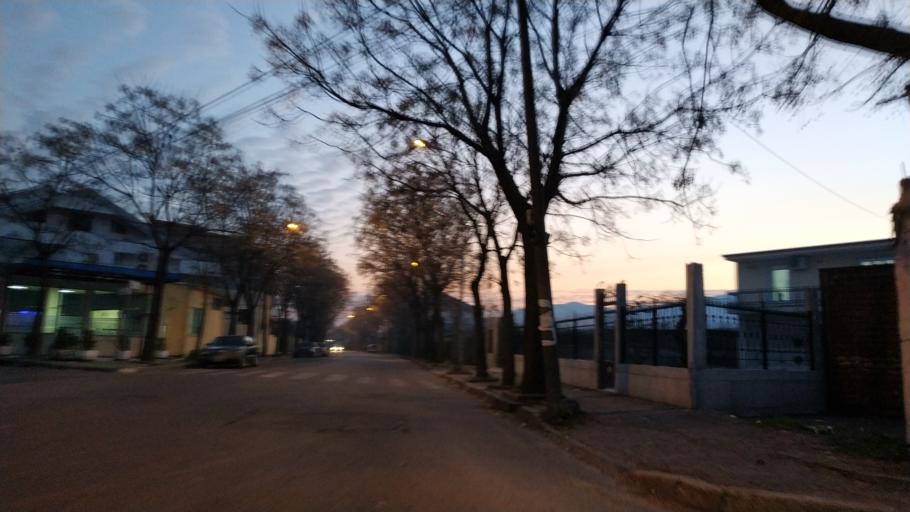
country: AL
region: Shkoder
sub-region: Rrethi i Shkodres
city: Shkoder
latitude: 42.0759
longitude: 19.5032
